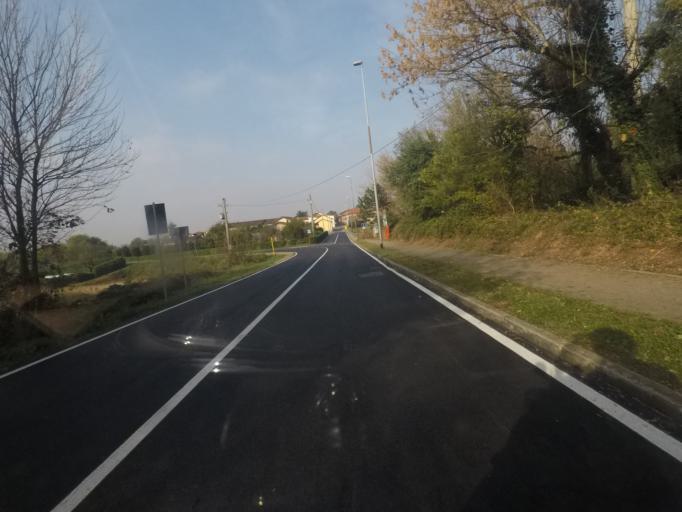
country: IT
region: Lombardy
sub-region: Provincia di Monza e Brianza
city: Aicurzio
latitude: 45.6318
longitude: 9.4129
